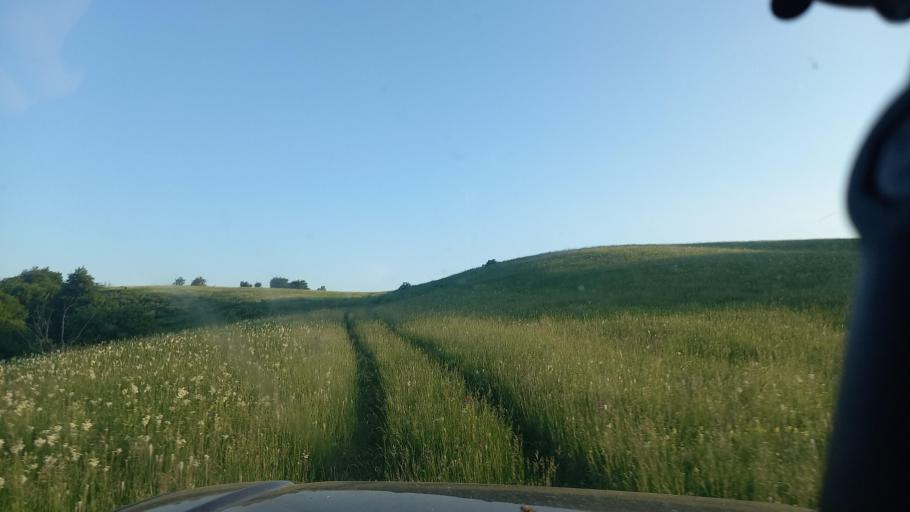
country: RU
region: Karachayevo-Cherkesiya
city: Kurdzhinovo
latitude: 44.1281
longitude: 41.0906
